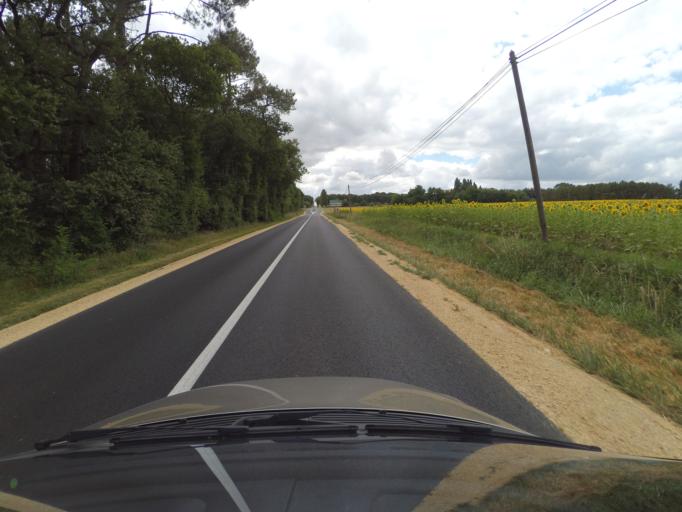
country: FR
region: Poitou-Charentes
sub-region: Departement de la Vienne
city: Saint-Gervais-les-Trois-Clochers
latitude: 46.9111
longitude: 0.4470
